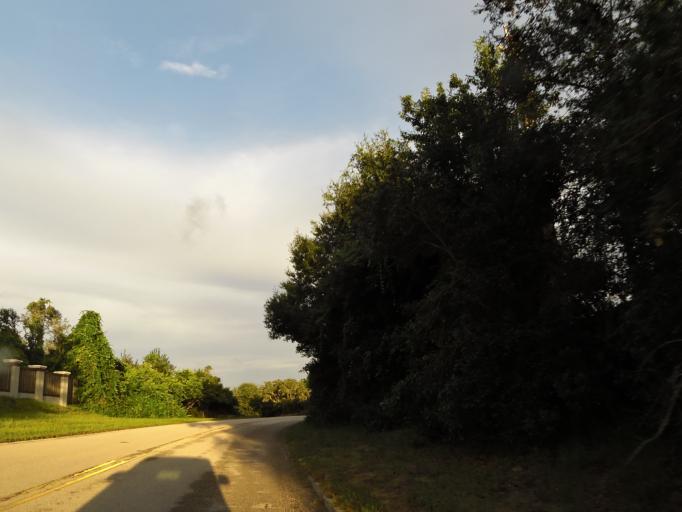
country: US
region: Florida
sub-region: Duval County
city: Atlantic Beach
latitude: 30.3794
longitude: -81.4963
